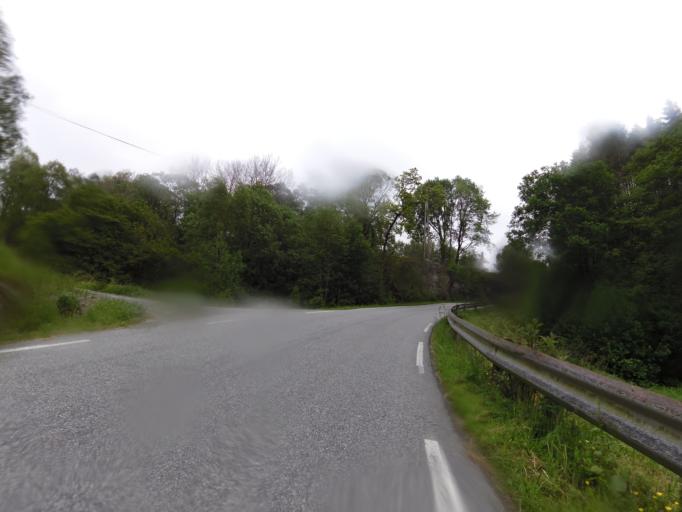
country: NO
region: Hordaland
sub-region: Sveio
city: Sveio
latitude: 59.5273
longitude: 5.2797
